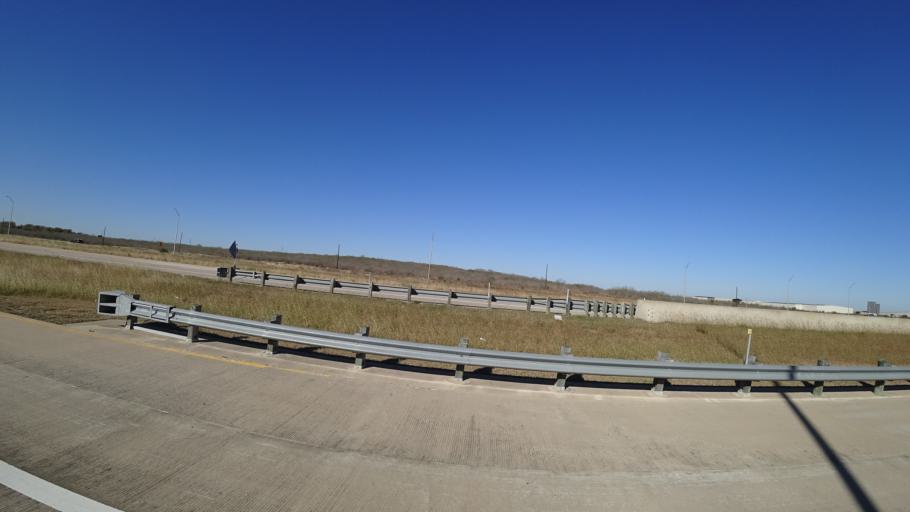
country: US
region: Texas
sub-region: Travis County
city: Onion Creek
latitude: 30.1101
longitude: -97.6637
